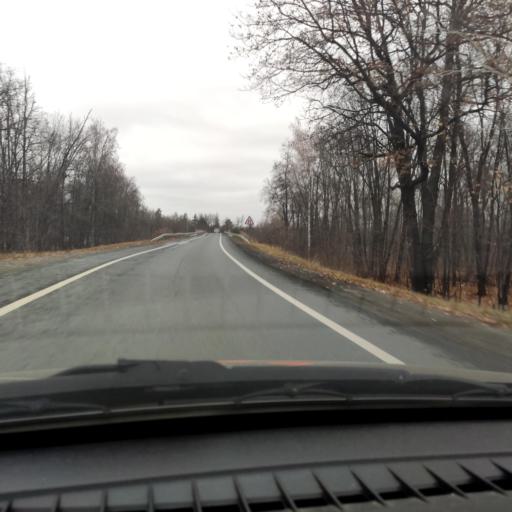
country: RU
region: Samara
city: Pribrezhnyy
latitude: 53.5104
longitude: 49.9305
